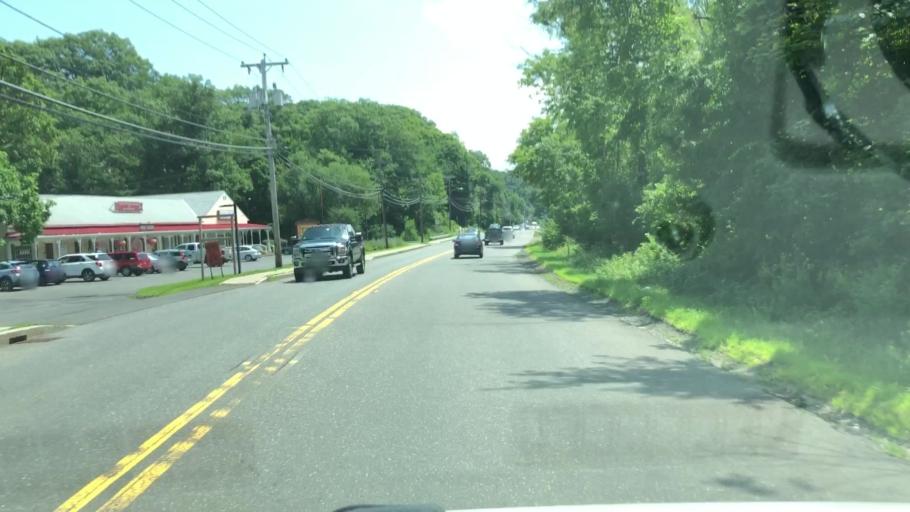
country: US
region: Massachusetts
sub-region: Hampshire County
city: Williamsburg
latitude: 42.3904
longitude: -72.7221
